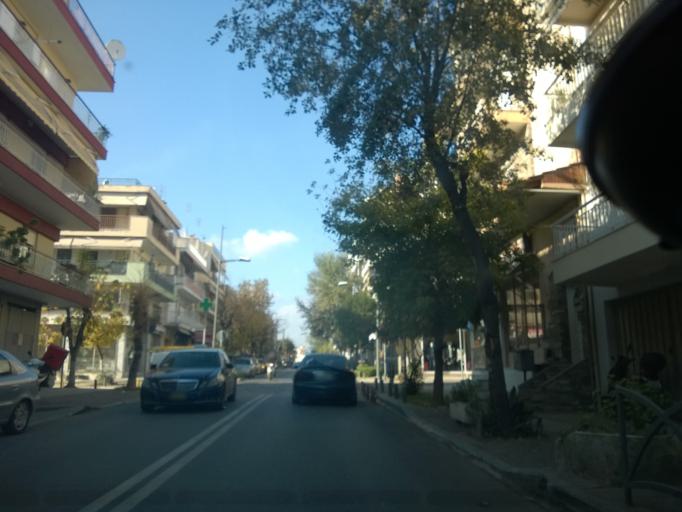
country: GR
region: Central Macedonia
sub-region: Nomos Thessalonikis
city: Stavroupoli
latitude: 40.6752
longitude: 22.9270
